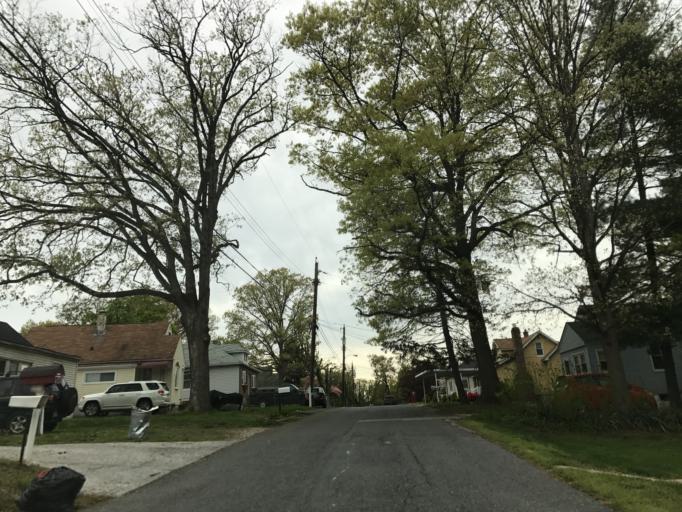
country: US
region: Maryland
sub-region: Baltimore County
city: Rosedale
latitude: 39.3150
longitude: -76.5055
